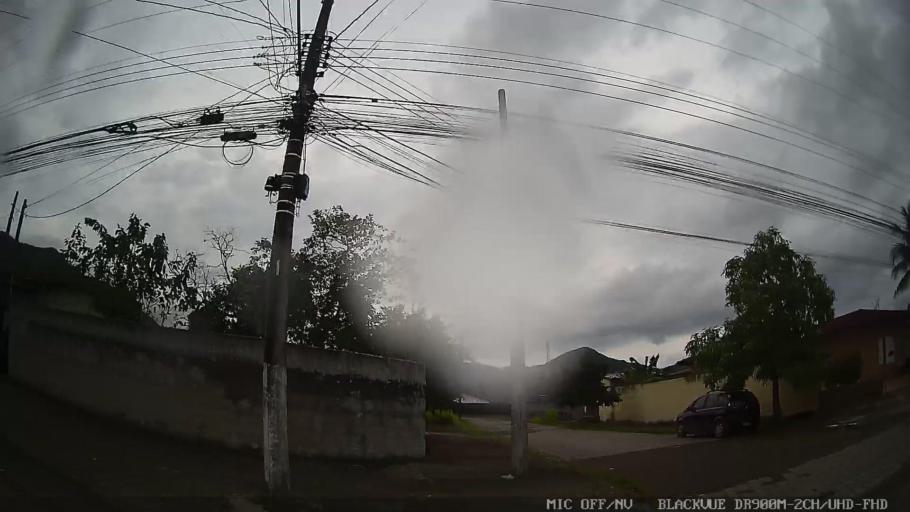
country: BR
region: Sao Paulo
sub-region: Caraguatatuba
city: Caraguatatuba
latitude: -23.6202
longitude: -45.3903
